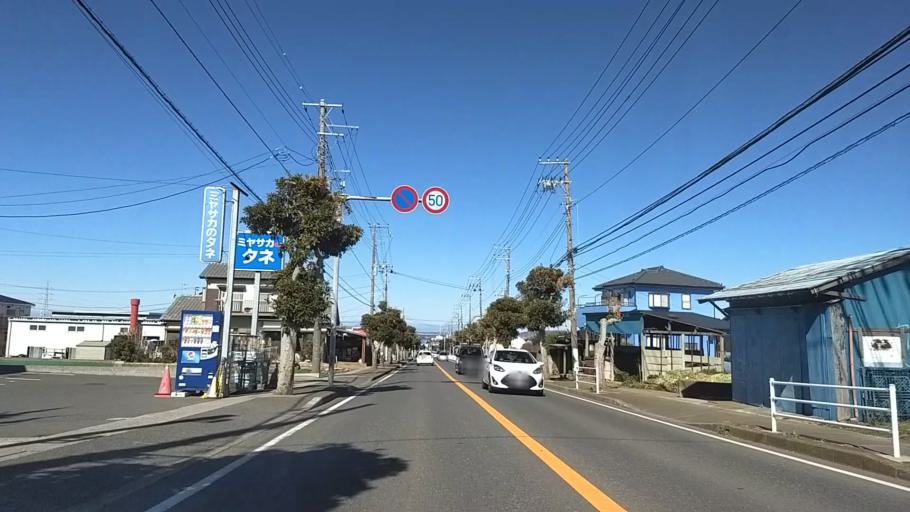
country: JP
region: Kanagawa
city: Miura
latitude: 35.1714
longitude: 139.6374
